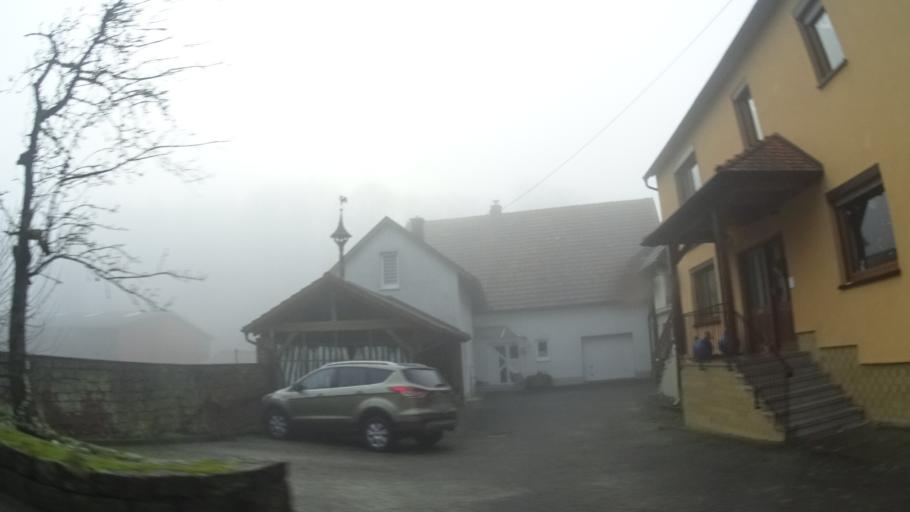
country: DE
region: Bavaria
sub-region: Regierungsbezirk Unterfranken
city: Neubrunn
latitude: 49.7430
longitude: 9.6088
